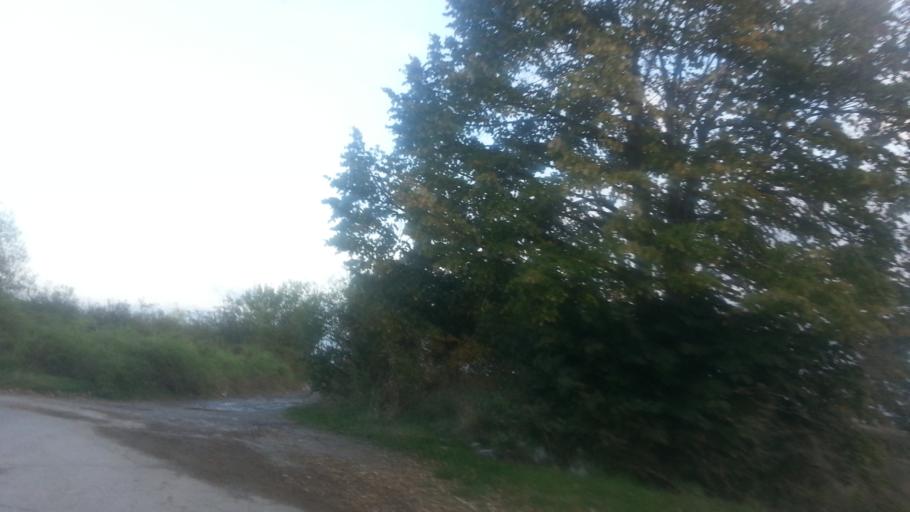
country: RS
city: Novi Banovci
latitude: 44.9202
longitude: 20.3196
